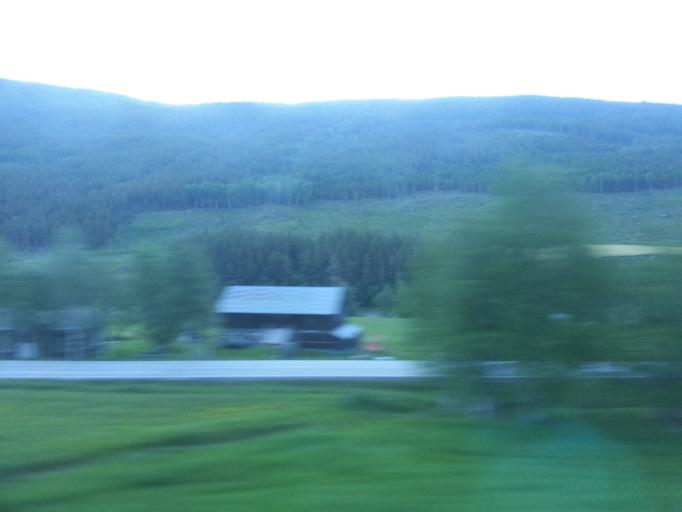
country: NO
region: Oppland
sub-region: Dovre
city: Dovre
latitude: 61.9071
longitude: 9.3646
